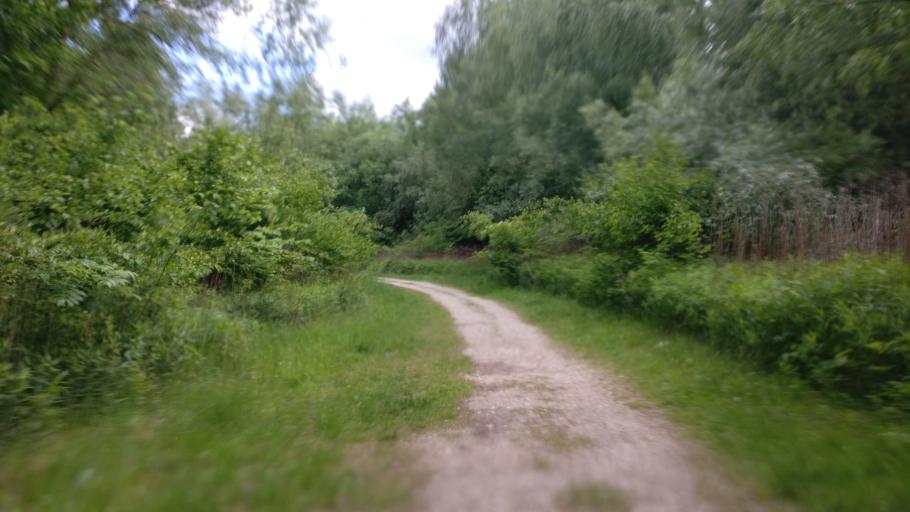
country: DE
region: North Rhine-Westphalia
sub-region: Regierungsbezirk Detmold
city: Lage
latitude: 52.0080
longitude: 8.7647
